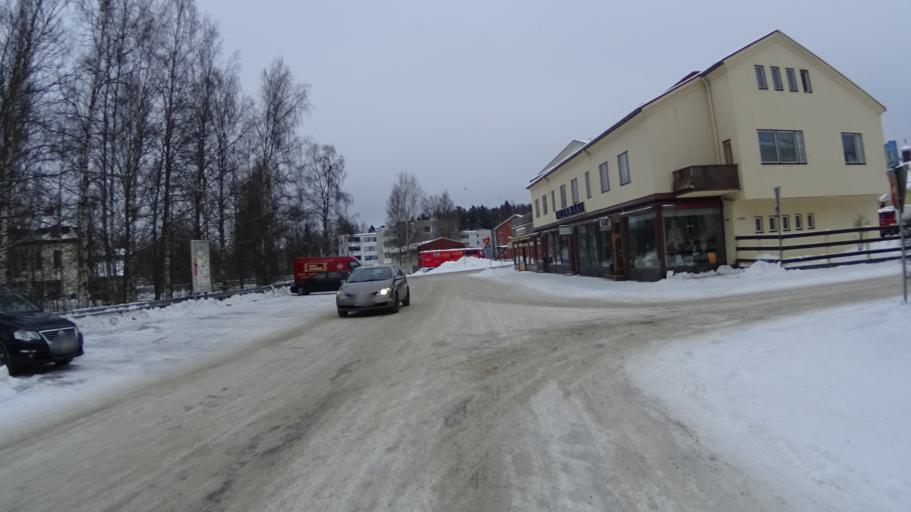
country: FI
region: Uusimaa
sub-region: Helsinki
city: Karkkila
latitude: 60.5344
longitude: 24.2076
